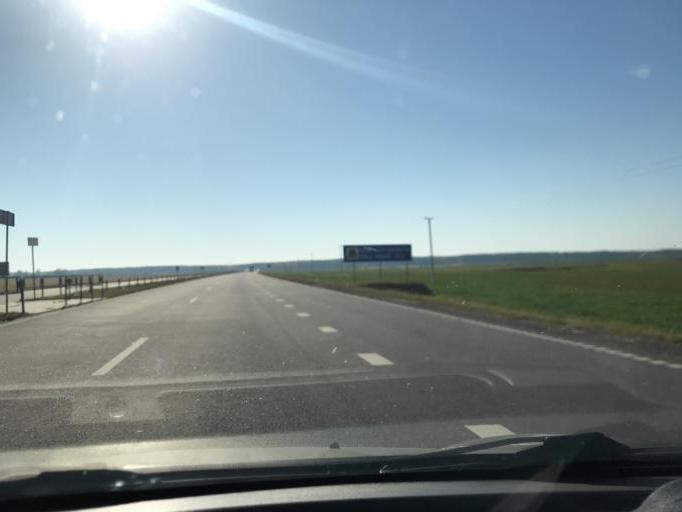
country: BY
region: Mogilev
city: Babruysk
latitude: 53.1727
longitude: 29.3600
